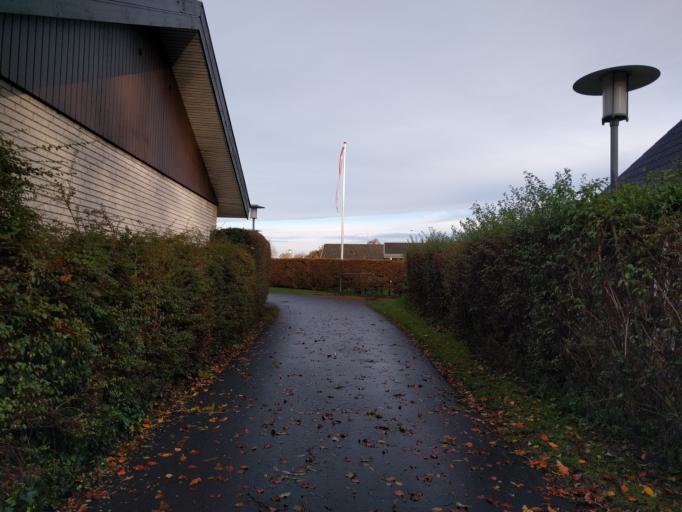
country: DK
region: South Denmark
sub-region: Fredericia Kommune
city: Snoghoj
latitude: 55.5339
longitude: 9.7251
